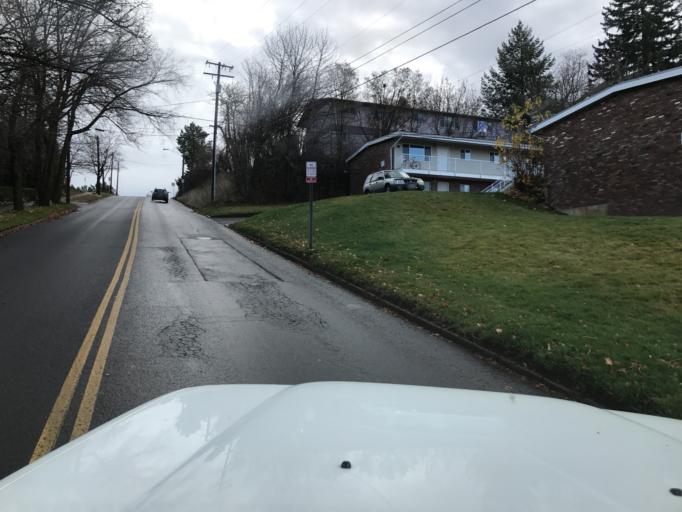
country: US
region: Idaho
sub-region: Latah County
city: Moscow
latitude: 46.7302
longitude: -116.9986
